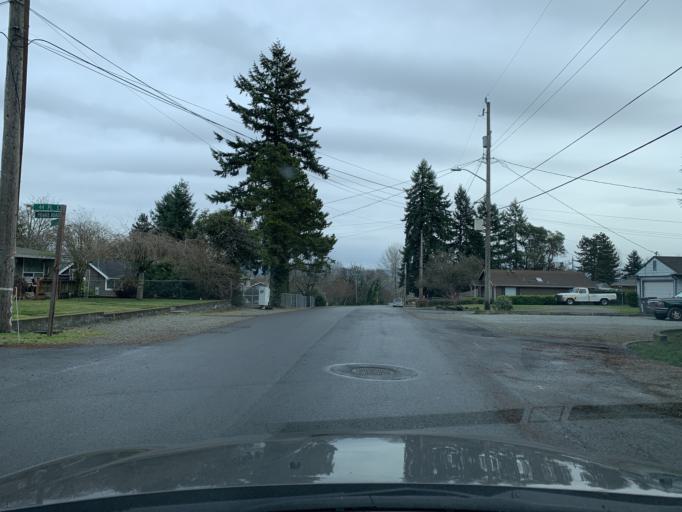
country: US
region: Washington
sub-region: King County
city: Tukwila
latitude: 47.4632
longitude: -122.2770
